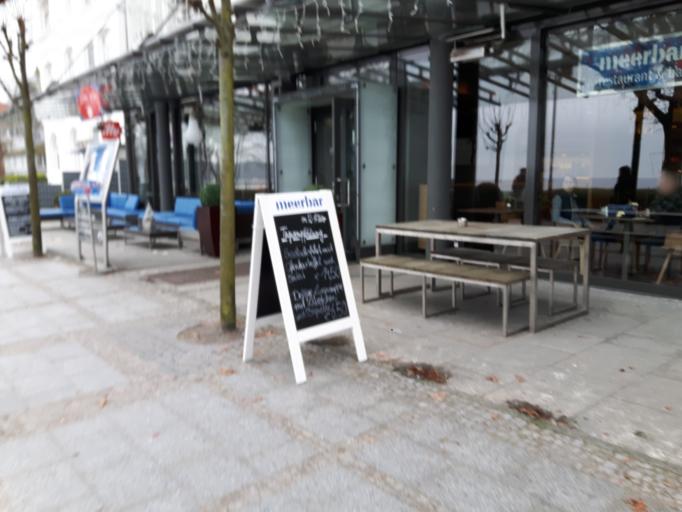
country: DE
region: Mecklenburg-Vorpommern
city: Ostseebad Binz
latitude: 54.4038
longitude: 13.6109
